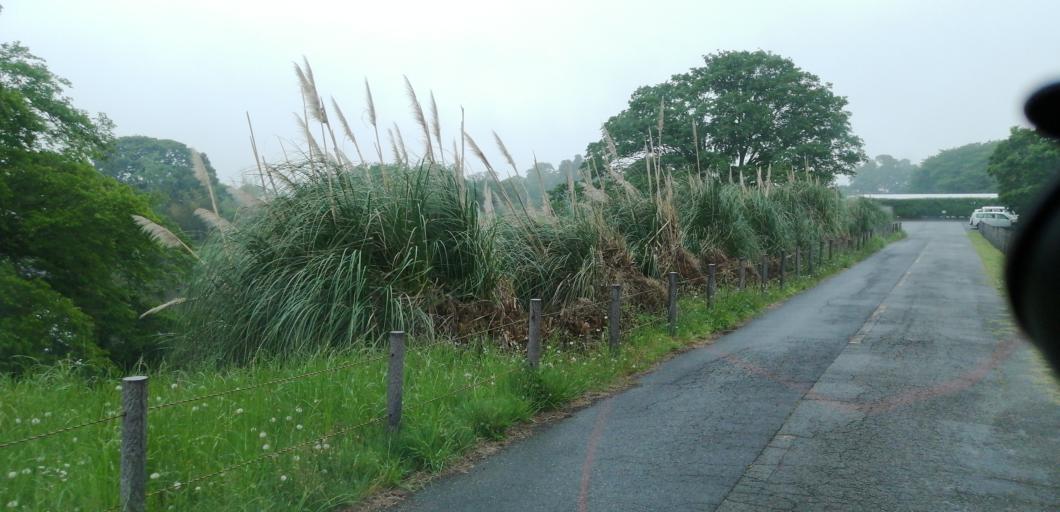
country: JP
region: Chiba
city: Ichihara
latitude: 35.4636
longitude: 140.1115
